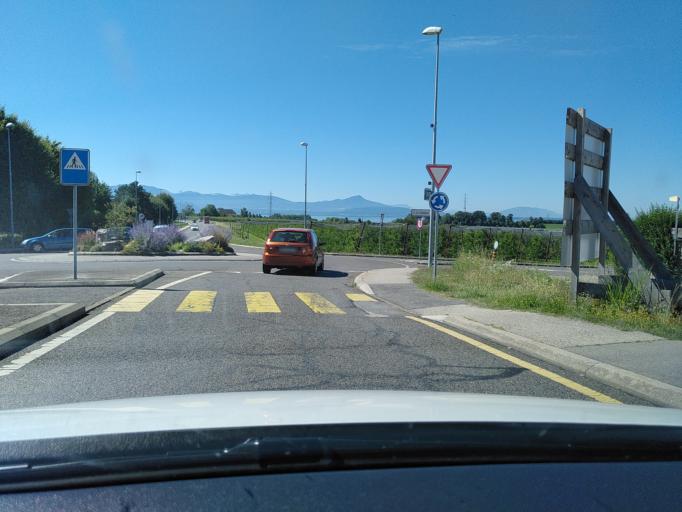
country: CH
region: Vaud
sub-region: Morges District
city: Aubonne
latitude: 46.4888
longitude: 6.3993
